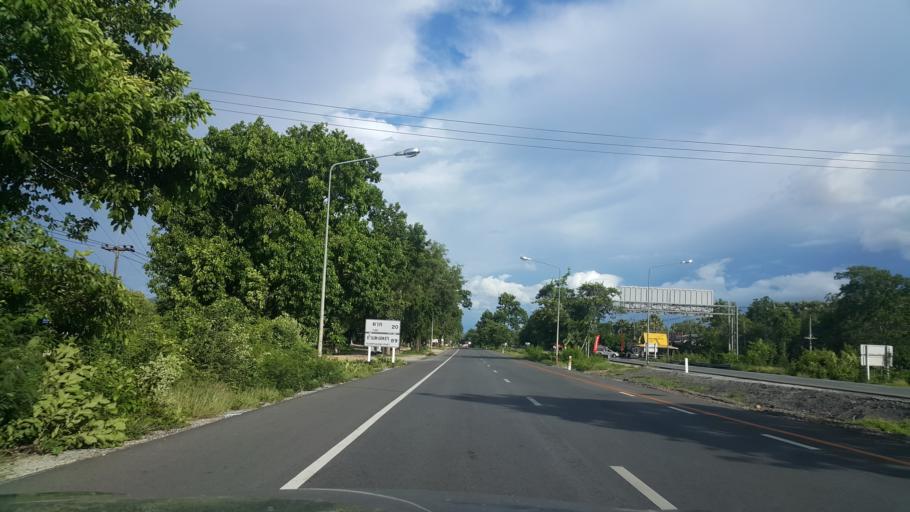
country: TH
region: Tak
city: Ban Tak
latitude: 17.0330
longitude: 99.0898
